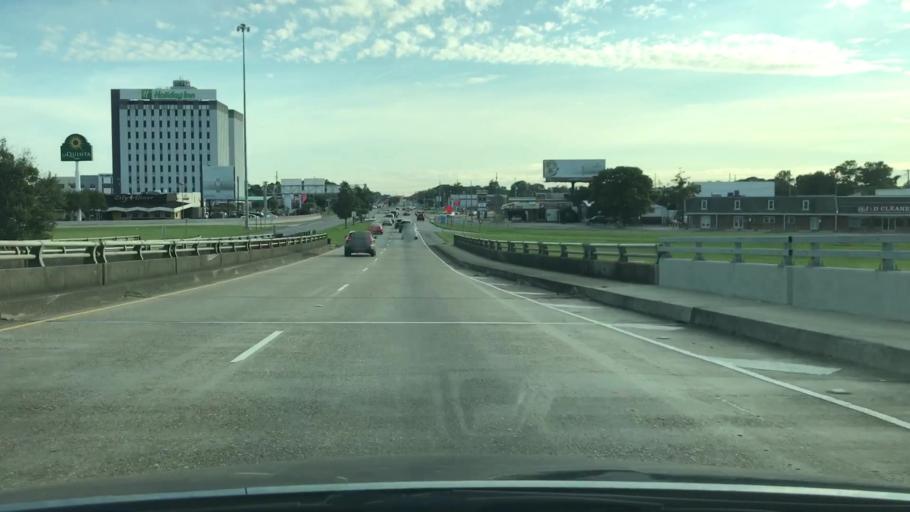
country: US
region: Louisiana
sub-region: Jefferson Parish
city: Metairie
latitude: 29.9962
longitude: -90.1556
